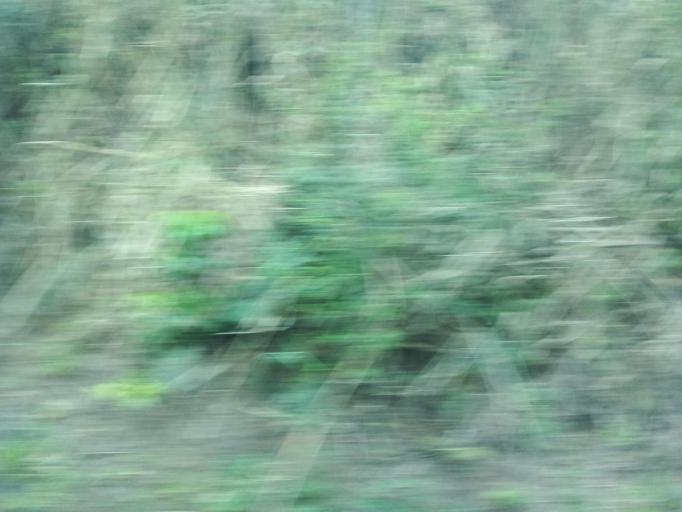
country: BR
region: Minas Gerais
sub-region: Rio Piracicaba
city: Rio Piracicaba
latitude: -19.9702
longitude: -43.2274
